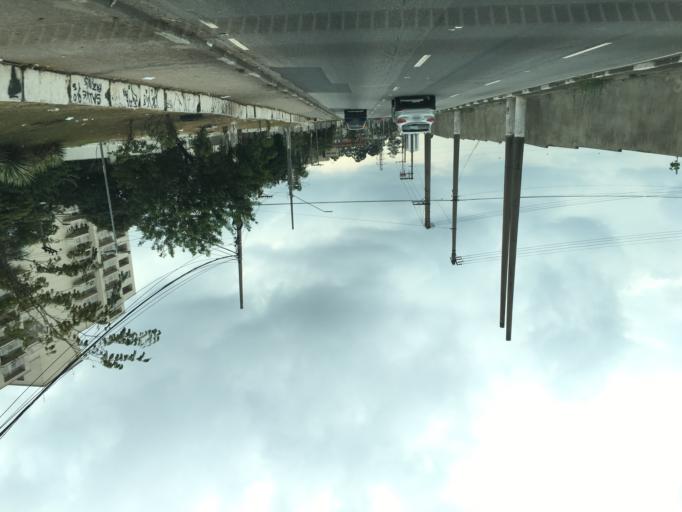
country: BR
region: Sao Paulo
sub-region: Osasco
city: Osasco
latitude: -23.5447
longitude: -46.7338
